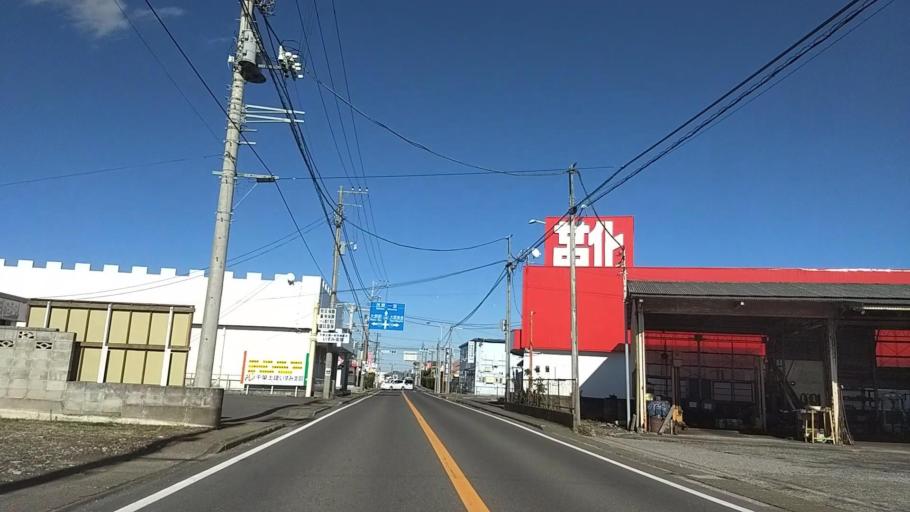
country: JP
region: Chiba
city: Ohara
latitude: 35.2481
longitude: 140.3950
